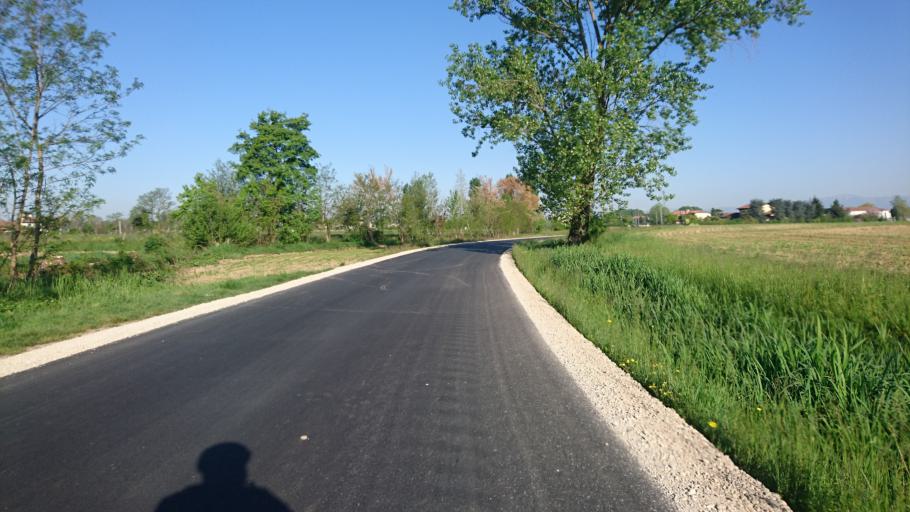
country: IT
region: Veneto
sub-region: Provincia di Padova
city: Massanzago-Ca' Baglioni-San Dono
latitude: 45.5437
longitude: 12.0042
